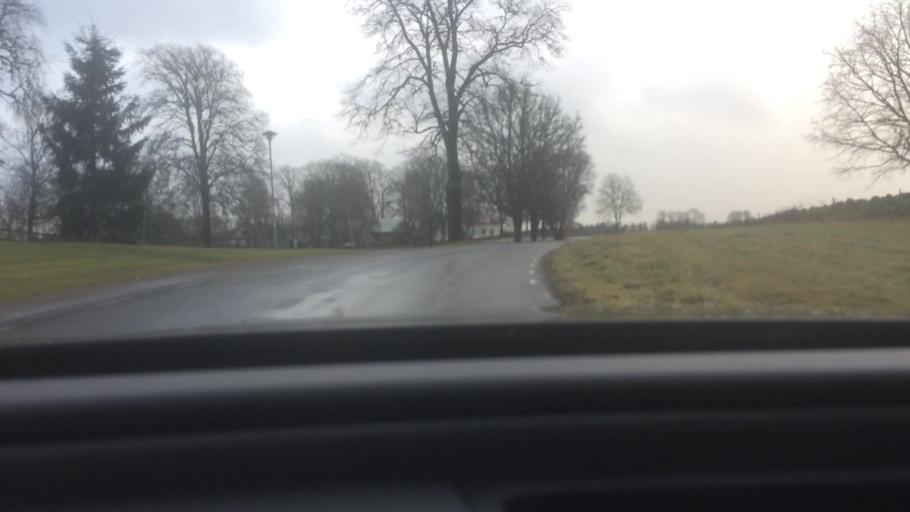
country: SE
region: Vaestra Goetaland
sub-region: Falkopings Kommun
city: Floby
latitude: 57.9925
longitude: 13.4666
